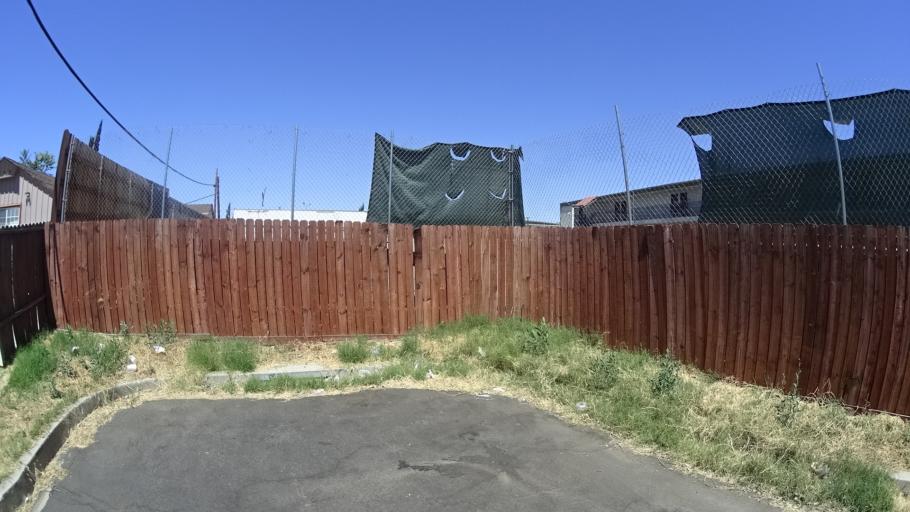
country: US
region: California
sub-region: Los Angeles County
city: San Fernando
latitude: 34.2628
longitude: -118.4686
